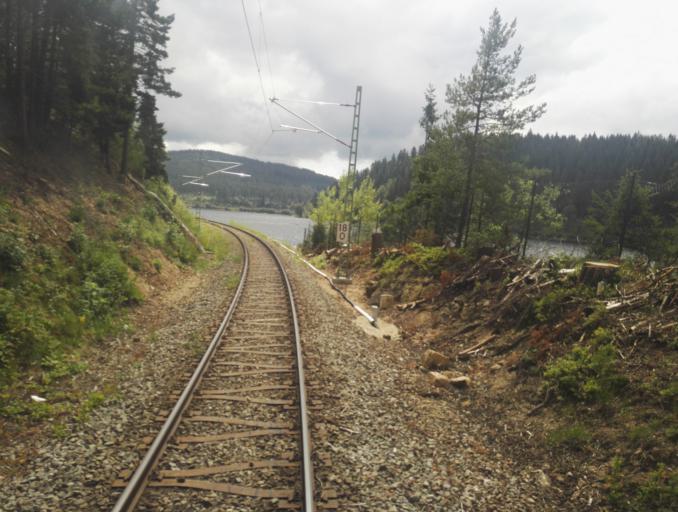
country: DE
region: Baden-Wuerttemberg
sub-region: Freiburg Region
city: Schluchsee
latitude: 47.8107
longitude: 8.1801
